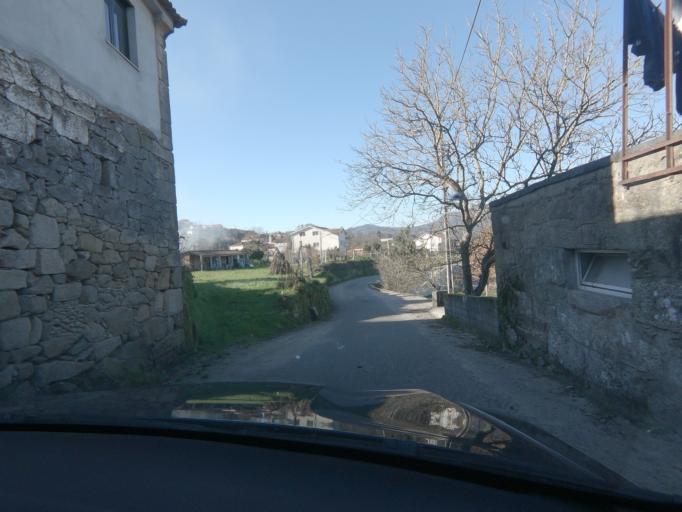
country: PT
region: Viseu
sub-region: Oliveira de Frades
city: Oliveira de Frades
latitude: 40.7332
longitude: -8.1575
